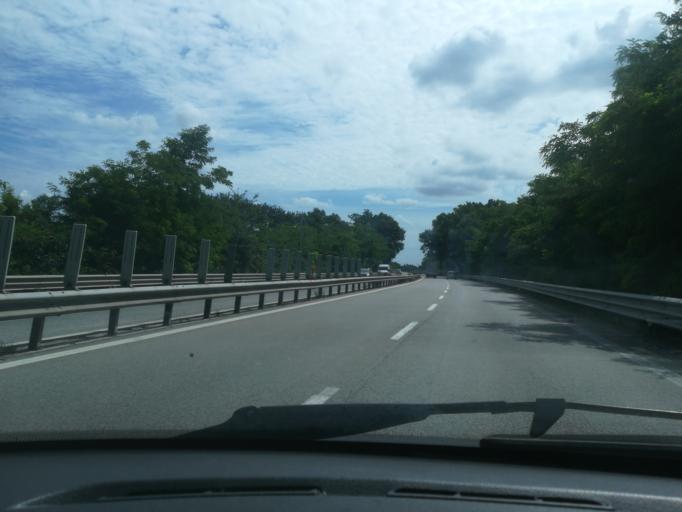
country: IT
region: The Marches
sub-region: Provincia di Macerata
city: Corridonia
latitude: 43.2642
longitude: 13.5356
